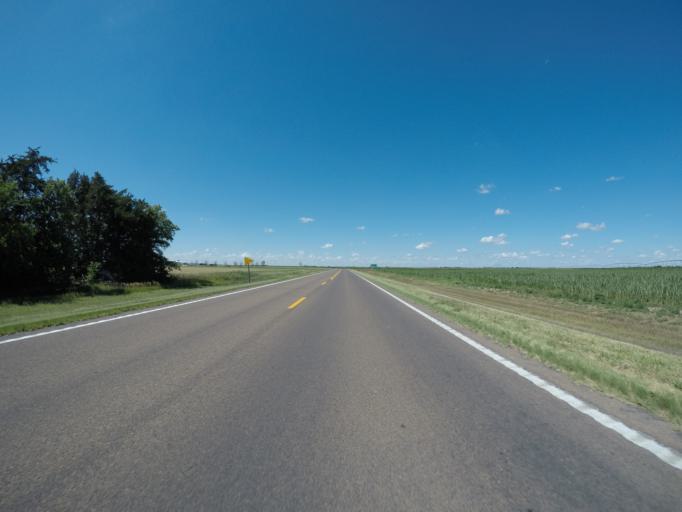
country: US
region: Nebraska
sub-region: Chase County
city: Imperial
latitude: 40.5323
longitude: -101.6432
